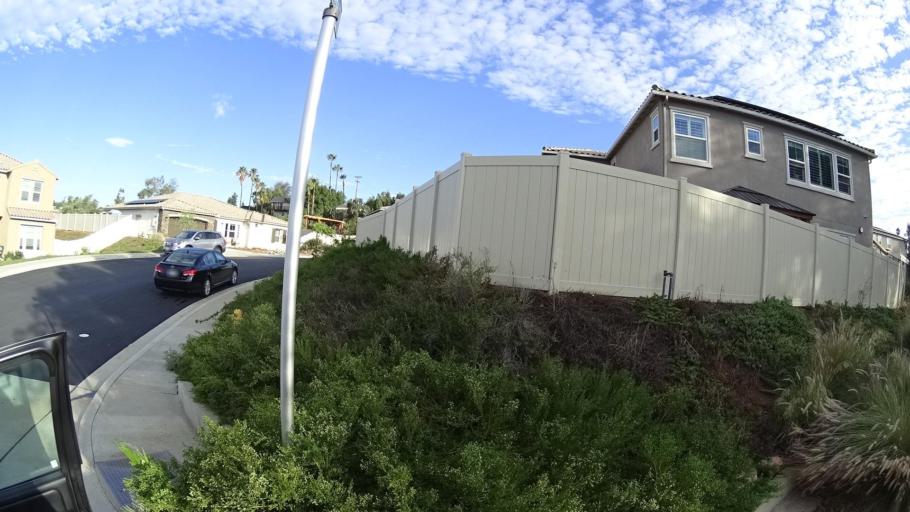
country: US
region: California
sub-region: San Diego County
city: Spring Valley
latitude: 32.7509
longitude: -116.9959
